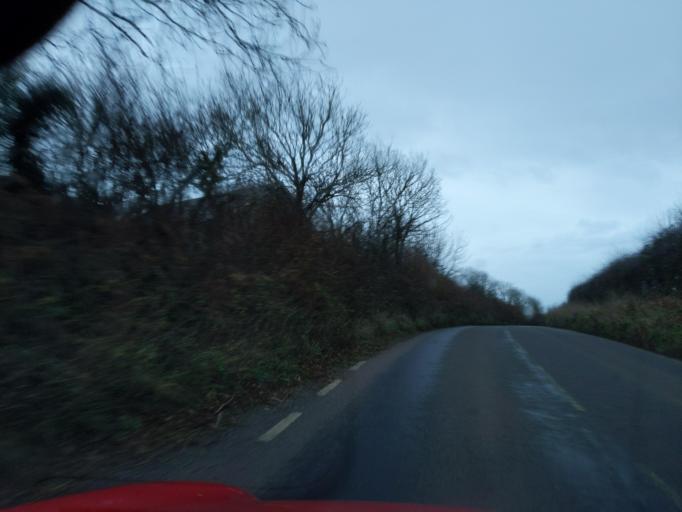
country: GB
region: England
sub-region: Devon
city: Wembury
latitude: 50.3352
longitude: -4.0702
